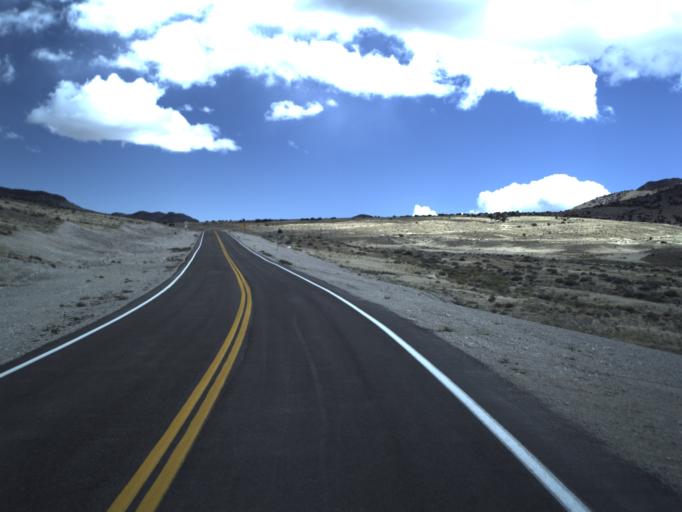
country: US
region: Utah
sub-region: Beaver County
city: Milford
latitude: 38.5055
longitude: -113.5962
